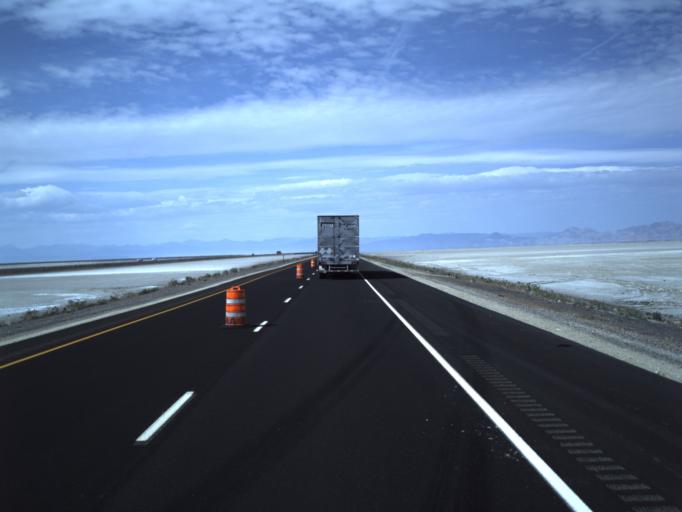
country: US
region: Utah
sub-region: Tooele County
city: Wendover
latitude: 40.7335
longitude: -113.5742
